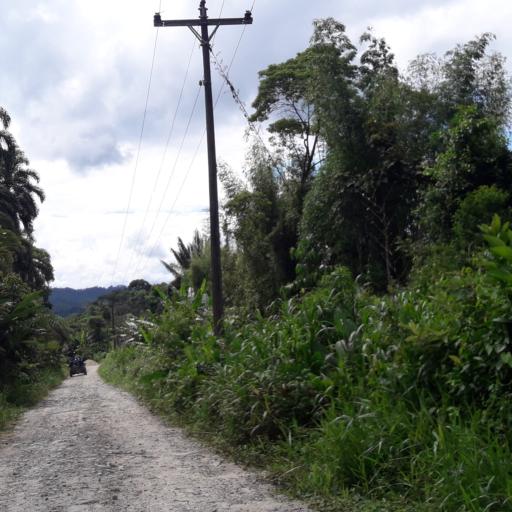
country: EC
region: Napo
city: Archidona
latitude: -0.9407
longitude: -77.8804
